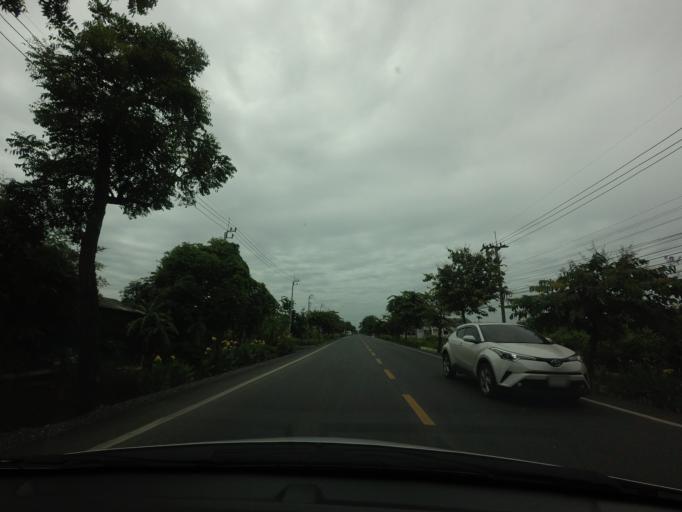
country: TH
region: Pathum Thani
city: Lam Luk Ka
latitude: 13.9021
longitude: 100.7937
